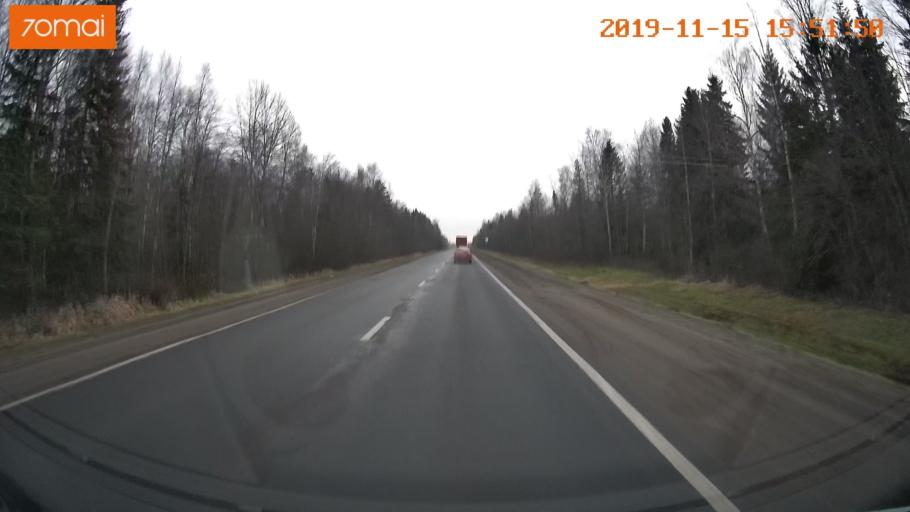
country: RU
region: Jaroslavl
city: Yaroslavl
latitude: 57.8899
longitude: 40.0045
